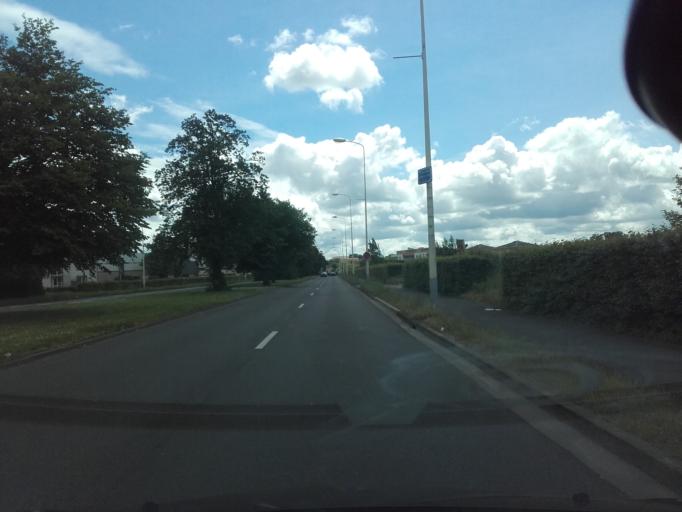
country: FR
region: Centre
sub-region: Departement d'Indre-et-Loire
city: Saint-Cyr-sur-Loire
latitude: 47.4228
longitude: 0.6994
